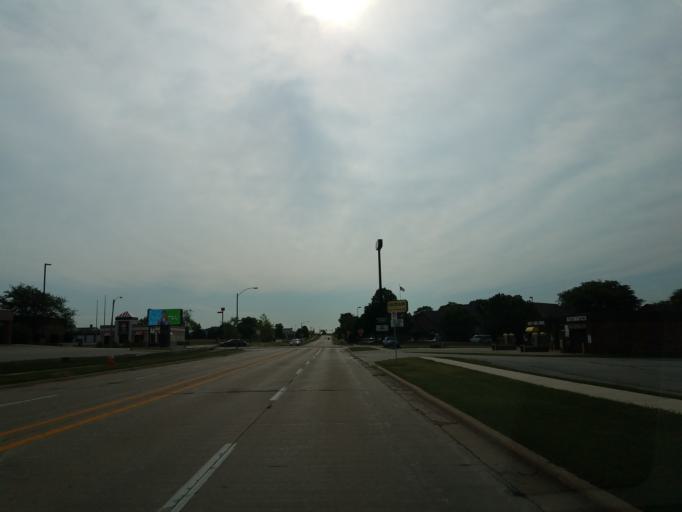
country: US
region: Illinois
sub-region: McLean County
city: Bloomington
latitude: 40.4841
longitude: -88.9505
